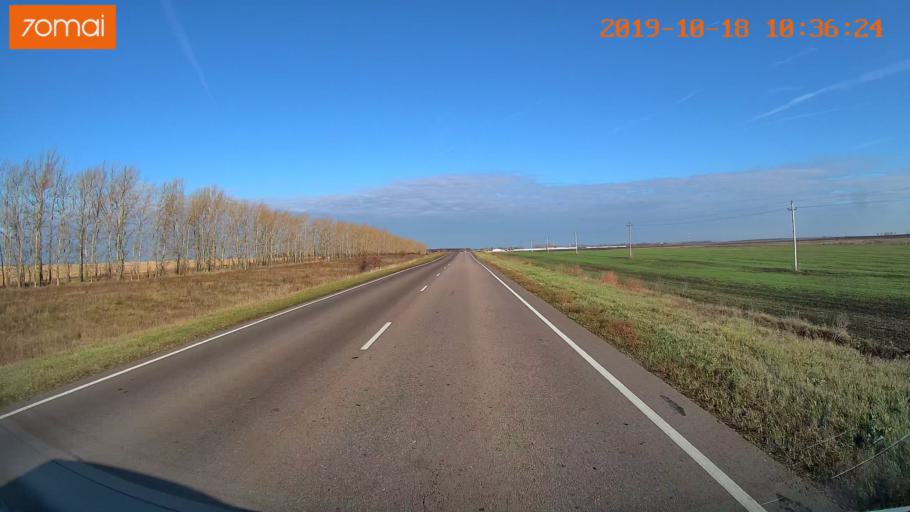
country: RU
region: Tula
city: Kurkino
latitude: 53.5480
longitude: 38.6256
